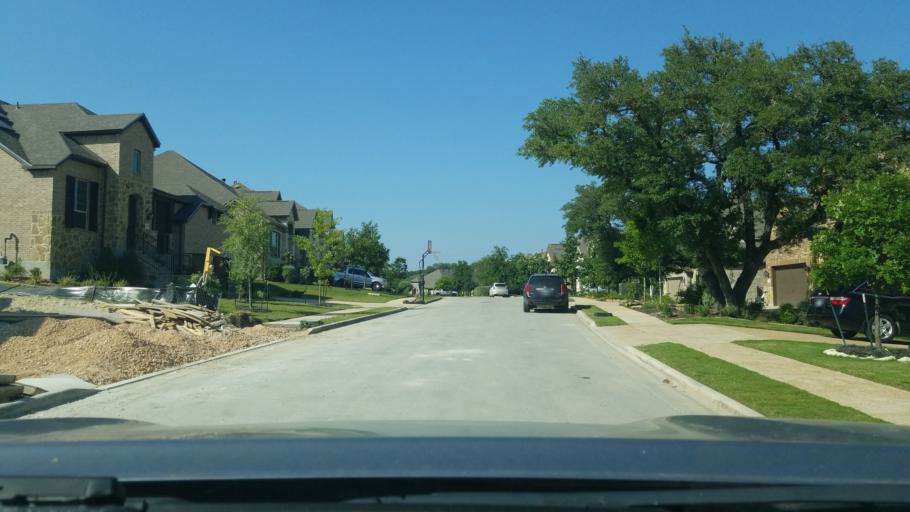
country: US
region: Texas
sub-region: Comal County
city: Bulverde
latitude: 29.7703
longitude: -98.4216
